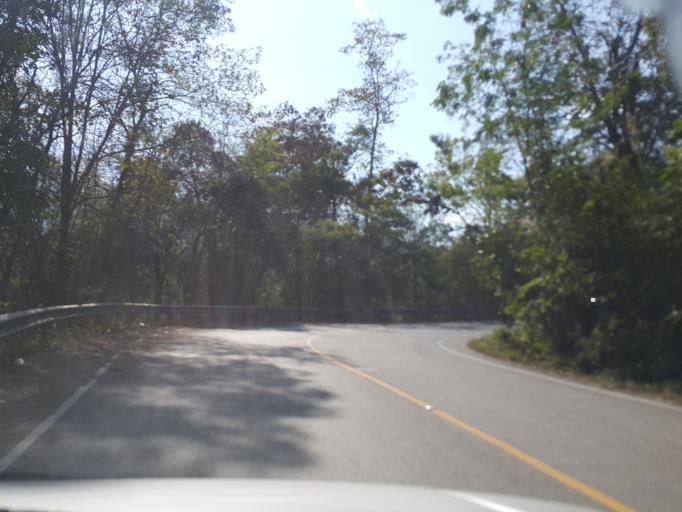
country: TH
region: Chiang Mai
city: Mae Wang
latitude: 18.6183
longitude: 98.7347
